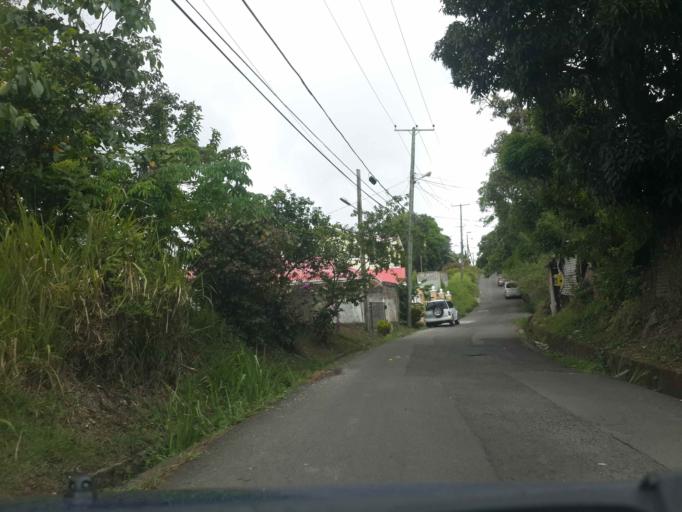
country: LC
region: Castries Quarter
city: Castries
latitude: 13.9965
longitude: -60.9899
